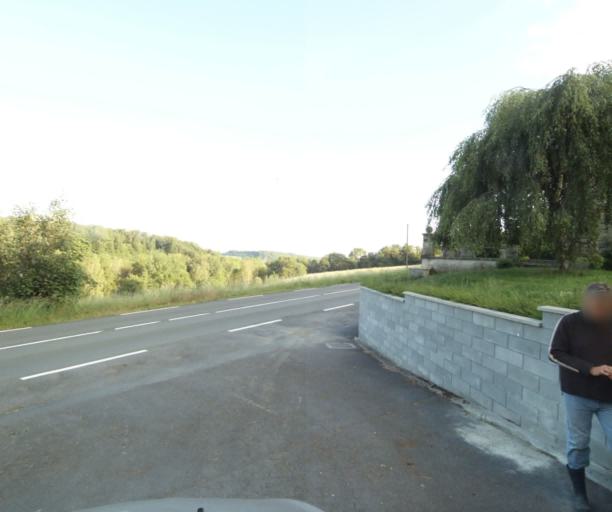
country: FR
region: Champagne-Ardenne
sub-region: Departement des Ardennes
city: Montcy-Notre-Dame
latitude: 49.7889
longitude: 4.7282
